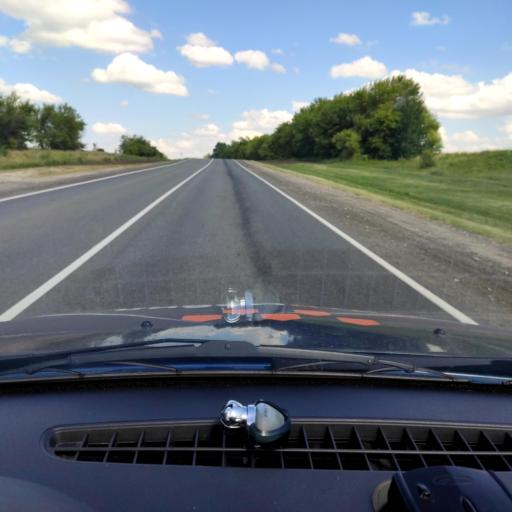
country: RU
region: Orjol
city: Livny
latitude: 52.4282
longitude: 37.7793
